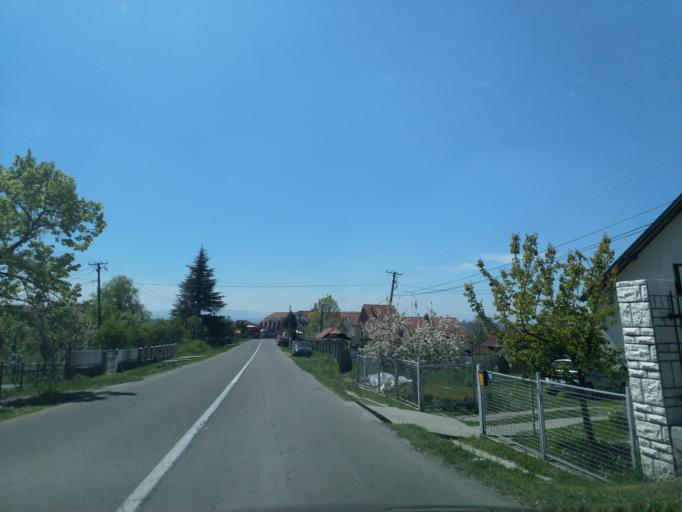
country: RS
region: Central Serbia
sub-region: Belgrade
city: Lazarevac
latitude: 44.3712
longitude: 20.3039
